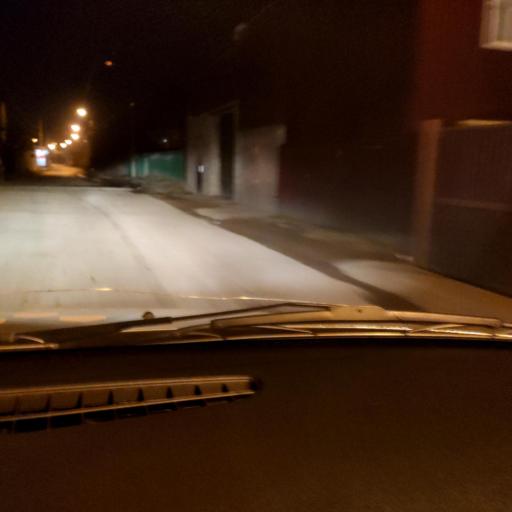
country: RU
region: Bashkortostan
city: Ufa
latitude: 54.7046
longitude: 55.9466
